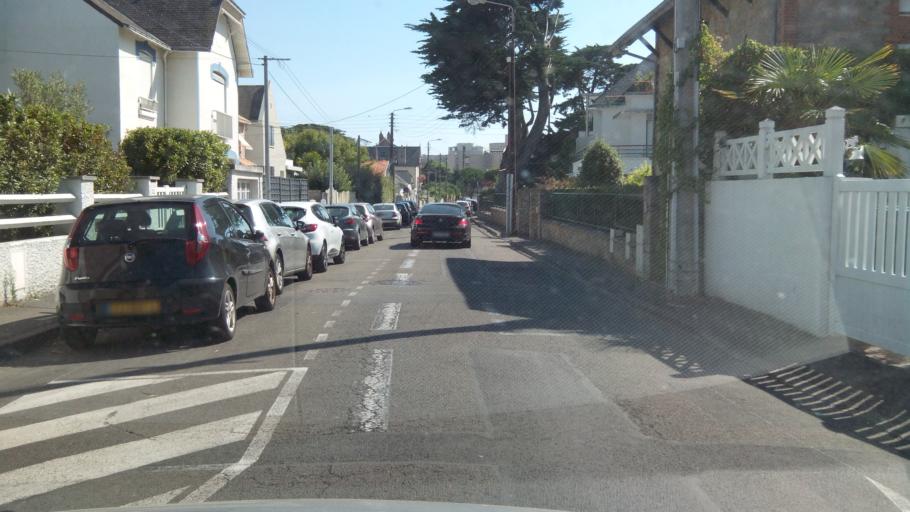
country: FR
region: Pays de la Loire
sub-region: Departement de la Loire-Atlantique
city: Pornichet
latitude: 47.2677
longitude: -2.3431
